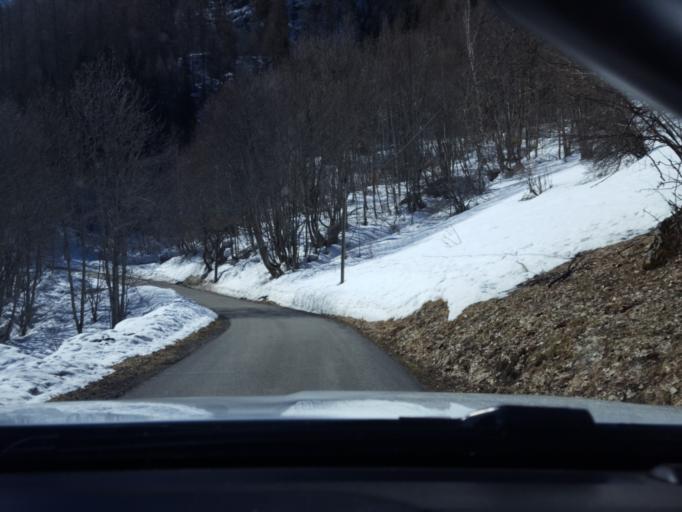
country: FR
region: Rhone-Alpes
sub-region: Departement de la Savoie
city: Valloire
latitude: 45.1752
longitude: 6.4274
